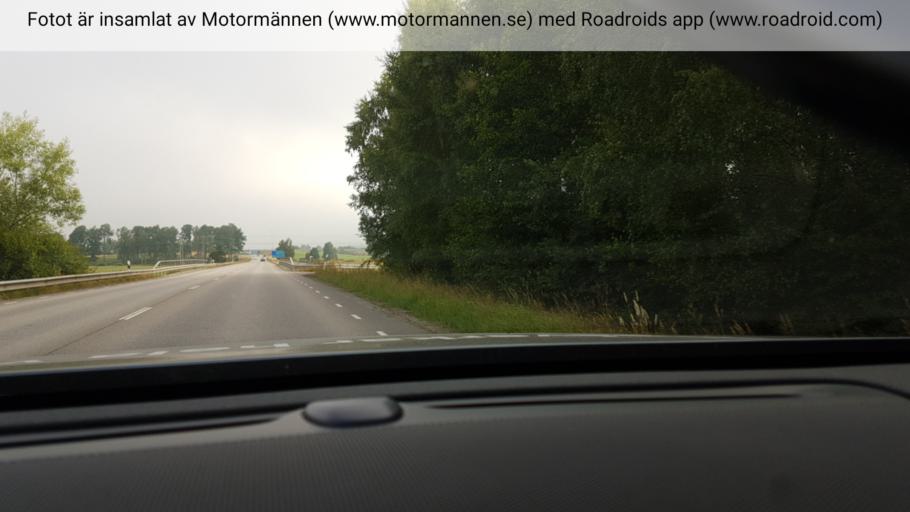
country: SE
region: Skane
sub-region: Hassleholms Kommun
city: Hassleholm
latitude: 56.1734
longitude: 13.7564
